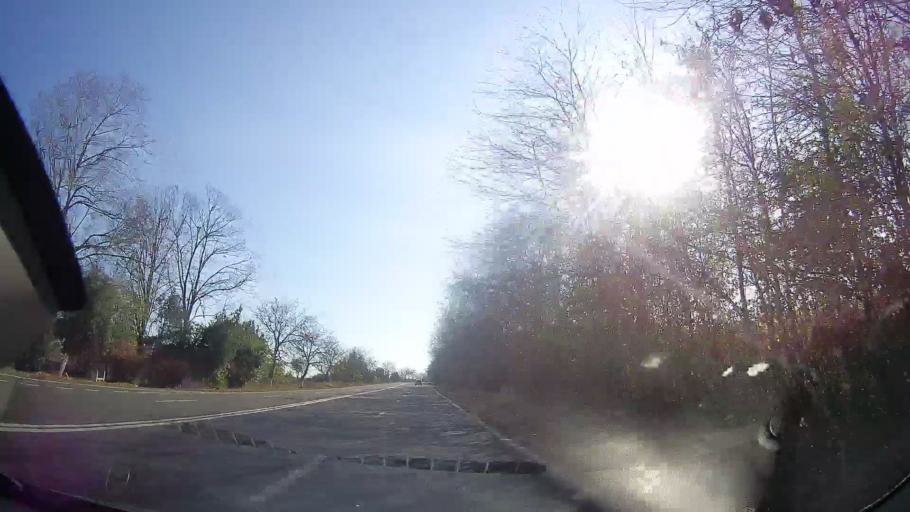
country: RO
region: Constanta
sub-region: Comuna Douazeci si Trei August
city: Dulcesti
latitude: 43.8893
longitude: 28.5727
